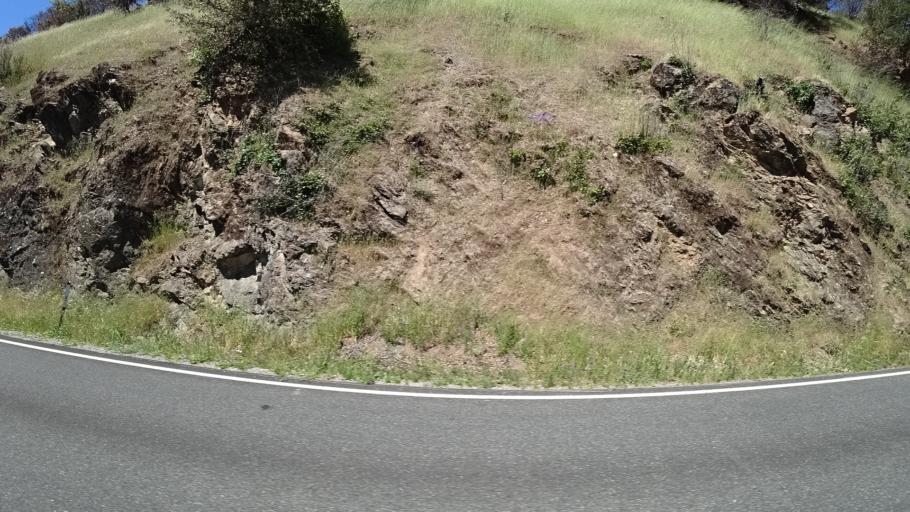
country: US
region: California
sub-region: Trinity County
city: Weaverville
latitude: 40.7663
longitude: -123.1082
